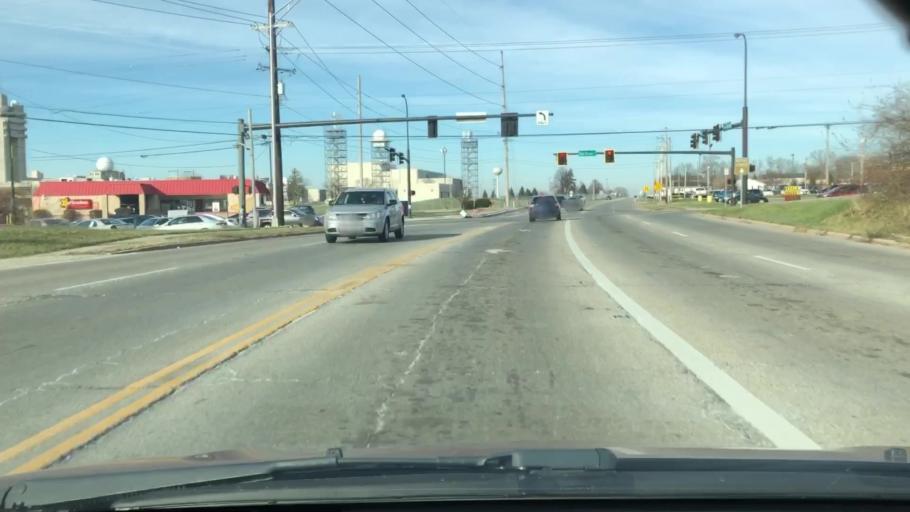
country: US
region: Ohio
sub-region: Greene County
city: Wright-Patterson AFB
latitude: 39.7741
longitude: -84.0797
